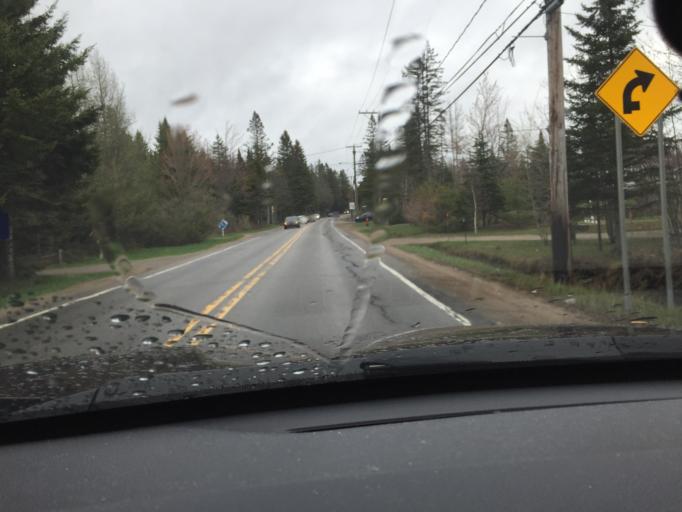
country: CA
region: Quebec
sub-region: Capitale-Nationale
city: Sainte Catherine de la Jacques Cartier
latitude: 46.8472
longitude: -71.5998
